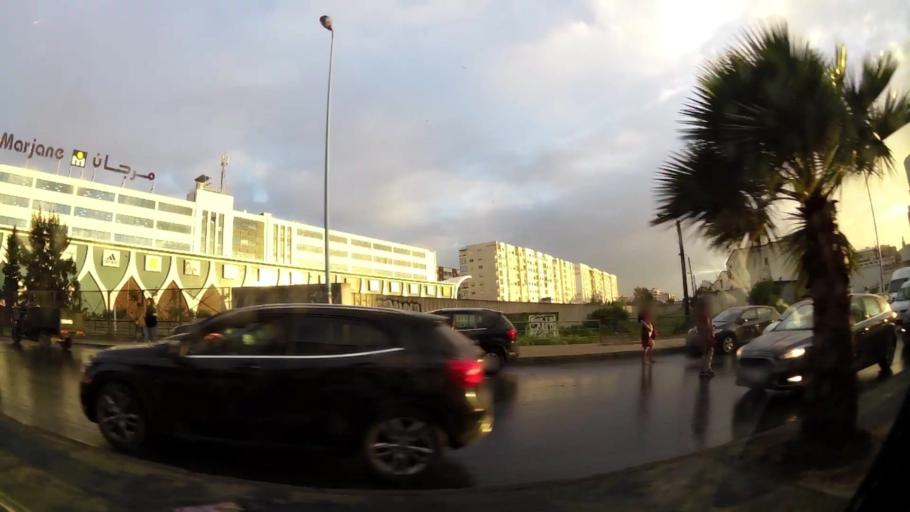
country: MA
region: Grand Casablanca
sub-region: Casablanca
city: Casablanca
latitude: 33.5870
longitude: -7.5935
